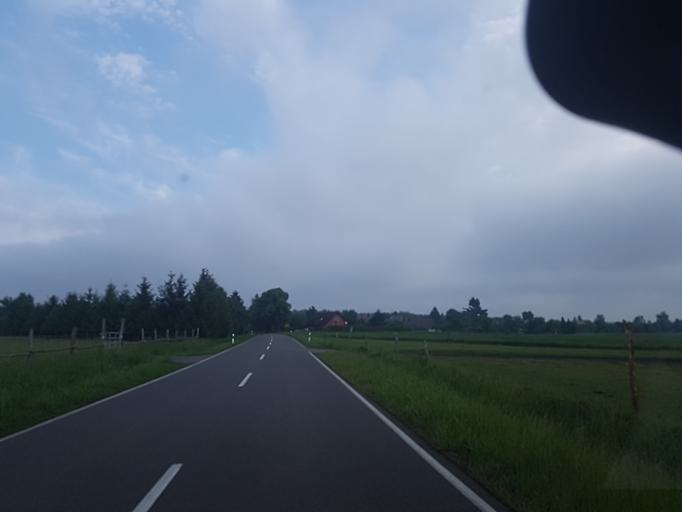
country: DE
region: Saxony-Anhalt
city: Klieken
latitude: 52.0060
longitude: 12.3722
